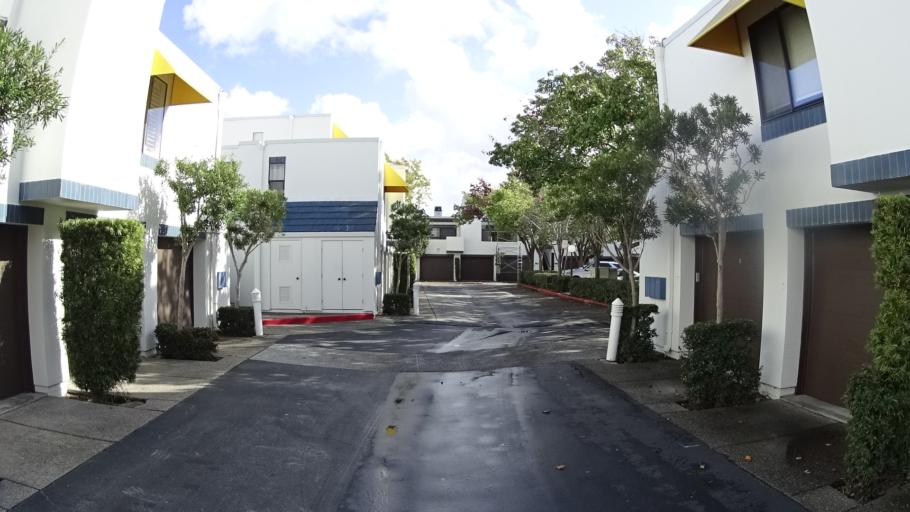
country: US
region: California
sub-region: San Mateo County
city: Foster City
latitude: 37.5532
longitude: -122.2707
